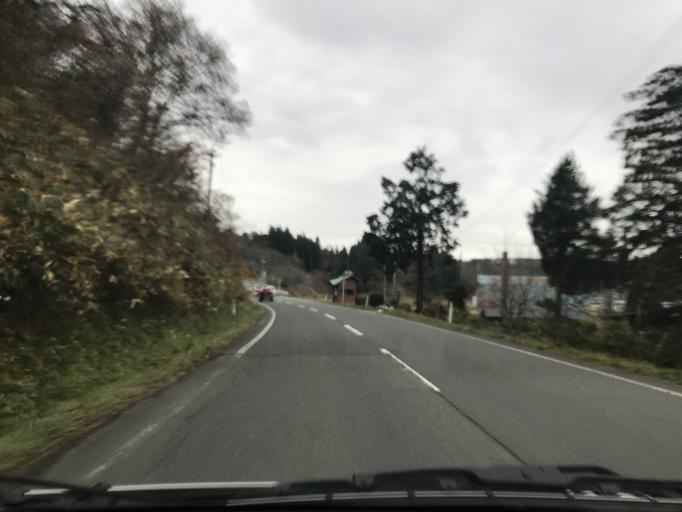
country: JP
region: Iwate
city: Mizusawa
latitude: 39.0347
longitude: 141.3393
